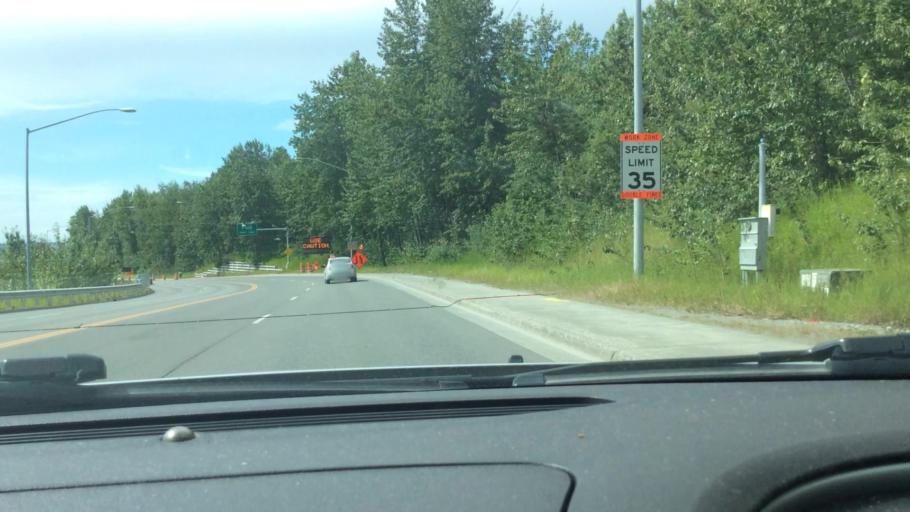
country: US
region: Alaska
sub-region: Anchorage Municipality
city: Anchorage
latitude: 61.2283
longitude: -149.8782
